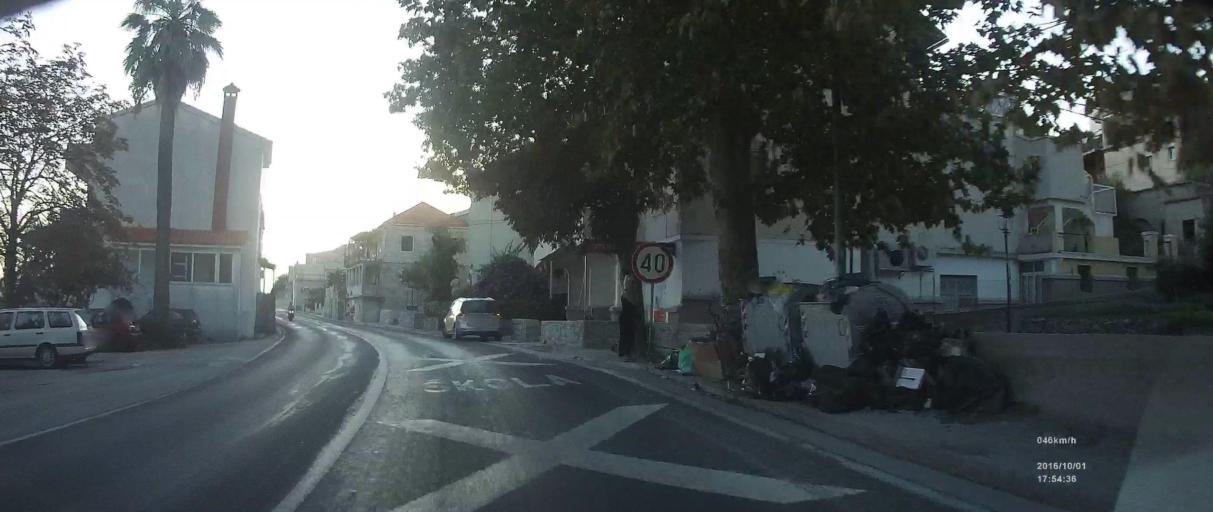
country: HR
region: Splitsko-Dalmatinska
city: Jesenice
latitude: 43.4614
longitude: 16.5987
